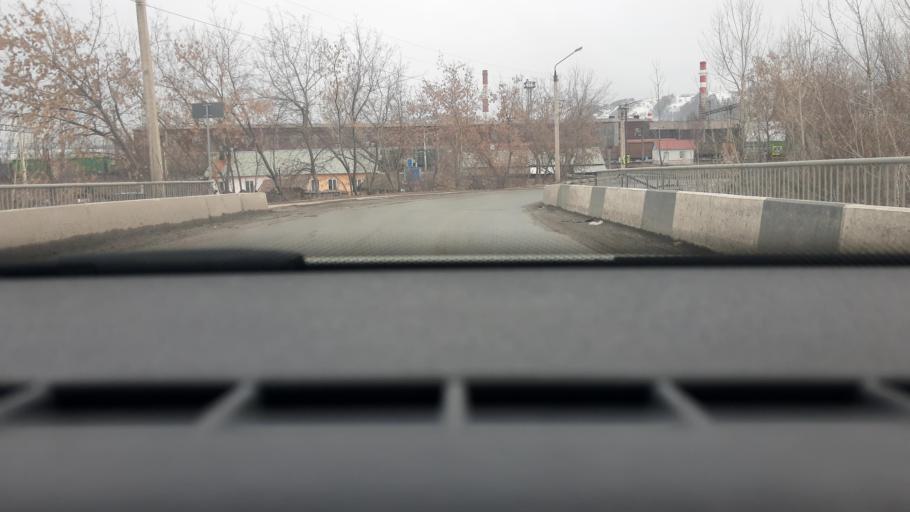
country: RU
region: Chelyabinsk
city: Asha
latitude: 54.9957
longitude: 57.2606
